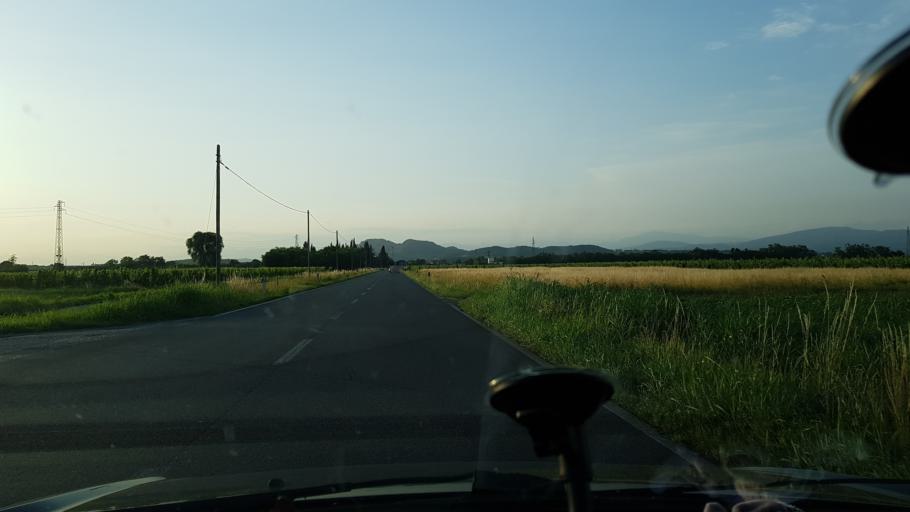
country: IT
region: Friuli Venezia Giulia
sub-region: Provincia di Gorizia
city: Moraro
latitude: 45.9193
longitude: 13.4998
